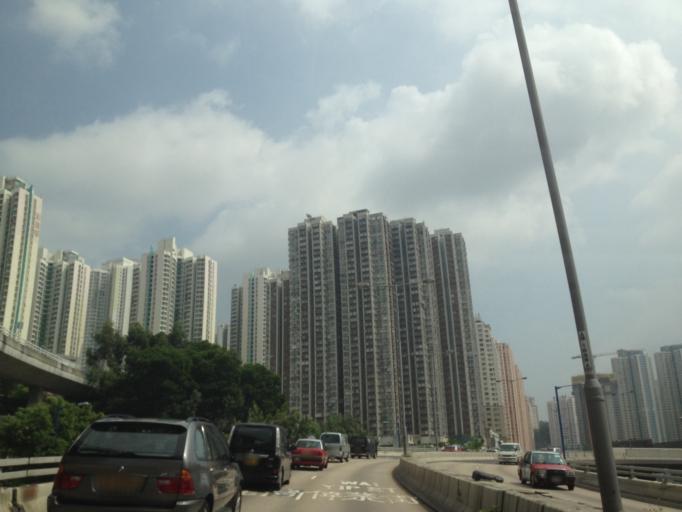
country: HK
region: Kowloon City
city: Kowloon
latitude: 22.3288
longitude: 114.2122
